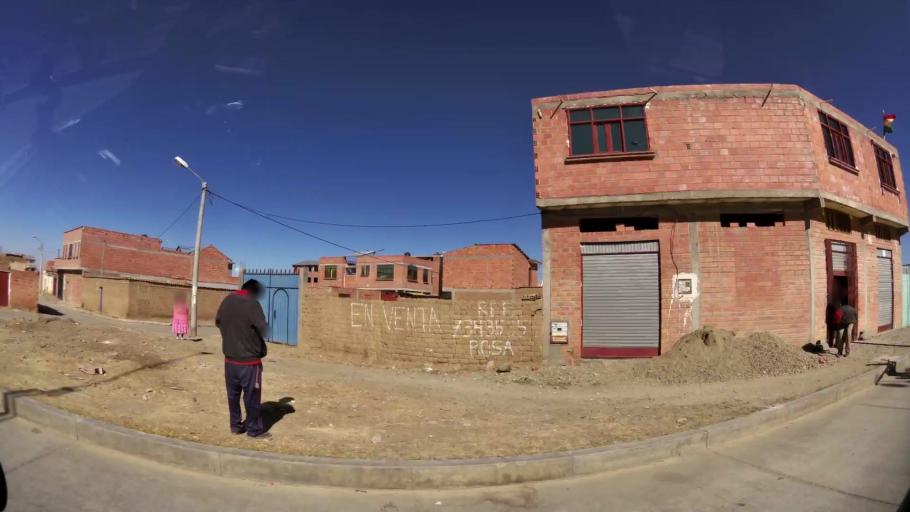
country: BO
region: La Paz
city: La Paz
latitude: -16.5289
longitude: -68.2205
